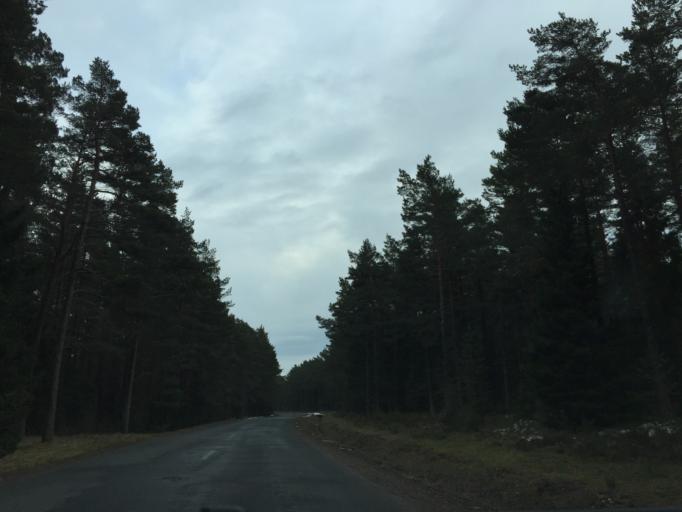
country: EE
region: Saare
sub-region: Kuressaare linn
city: Kuressaare
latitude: 58.4371
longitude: 22.0625
